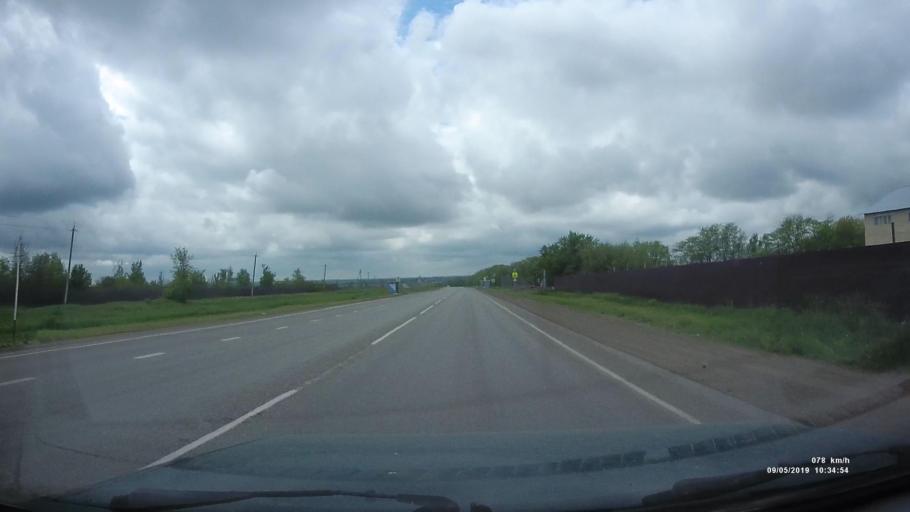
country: RU
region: Rostov
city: Peshkovo
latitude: 47.0490
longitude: 39.4165
